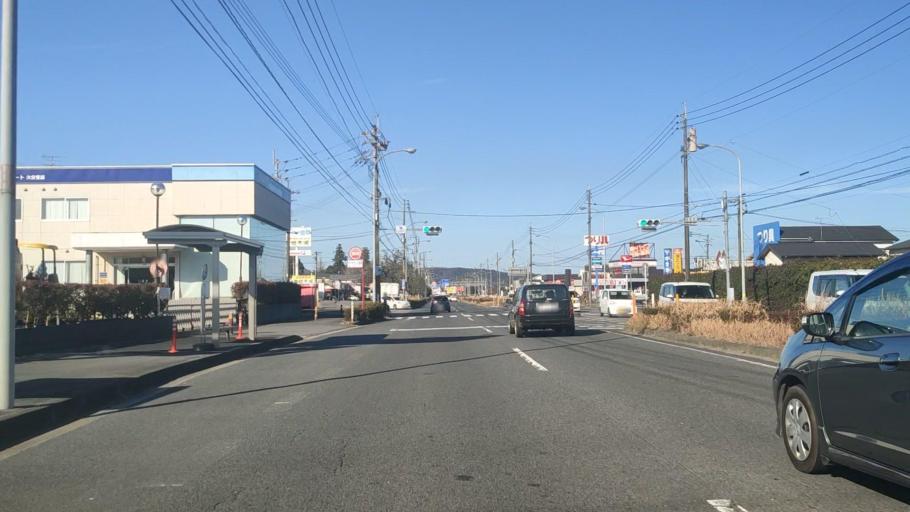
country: JP
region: Oita
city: Oita
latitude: 33.1435
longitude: 131.6579
